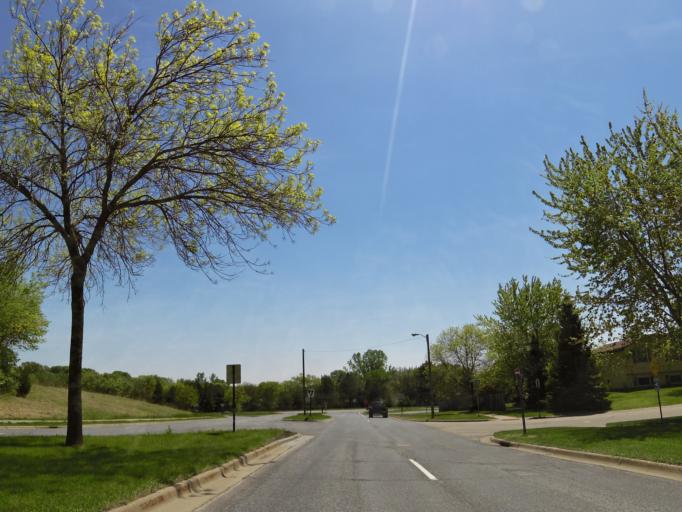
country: US
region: Minnesota
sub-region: Scott County
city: Savage
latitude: 44.8201
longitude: -93.3935
